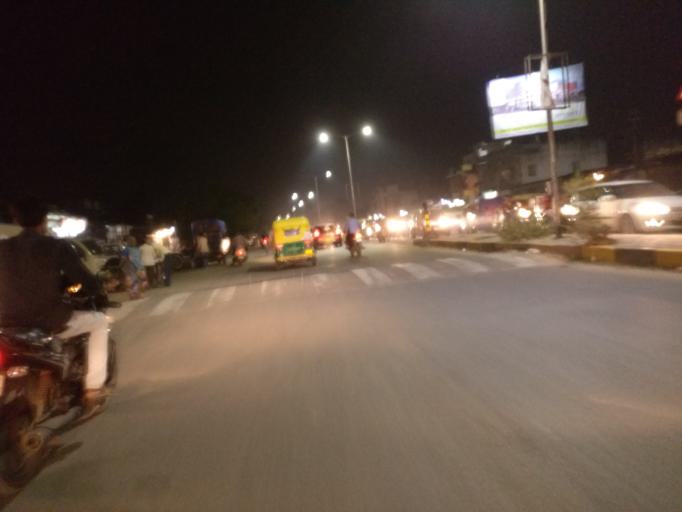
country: IN
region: Gujarat
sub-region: Ahmadabad
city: Sarkhej
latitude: 22.9985
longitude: 72.5435
